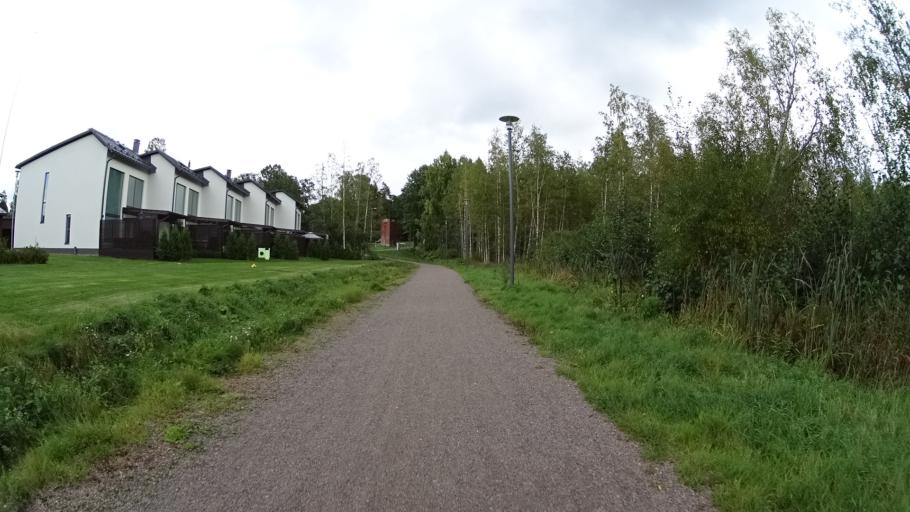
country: FI
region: Uusimaa
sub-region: Helsinki
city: Kauniainen
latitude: 60.2386
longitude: 24.7405
